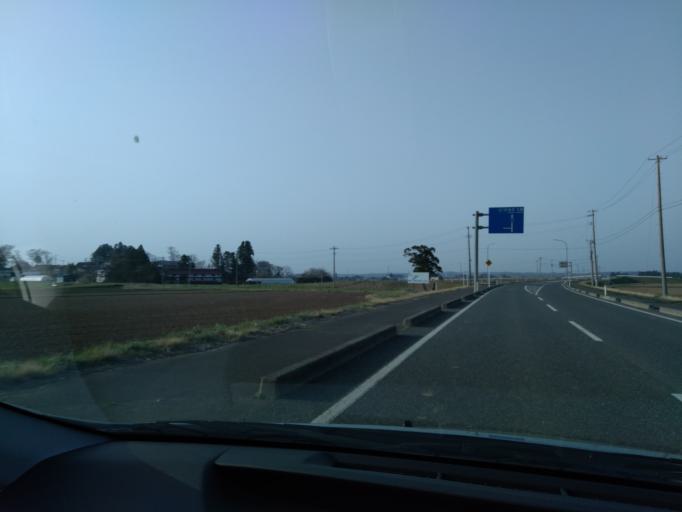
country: JP
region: Iwate
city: Ichinoseki
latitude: 38.7448
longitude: 141.1313
